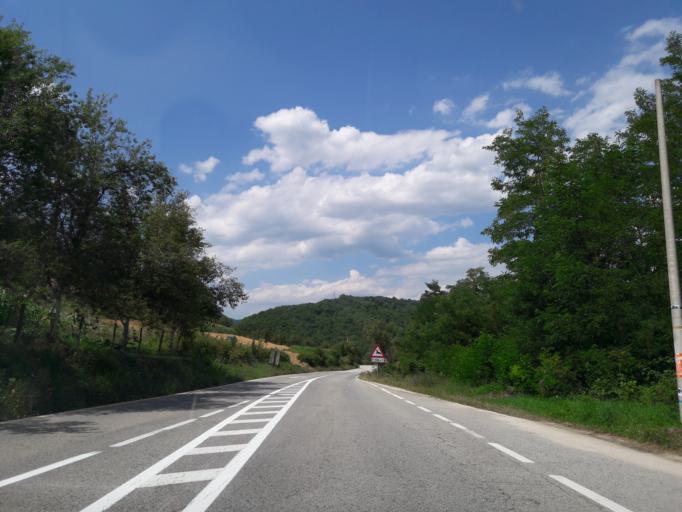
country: BA
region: Republika Srpska
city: Mrkonjic Grad
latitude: 44.5364
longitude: 17.1493
